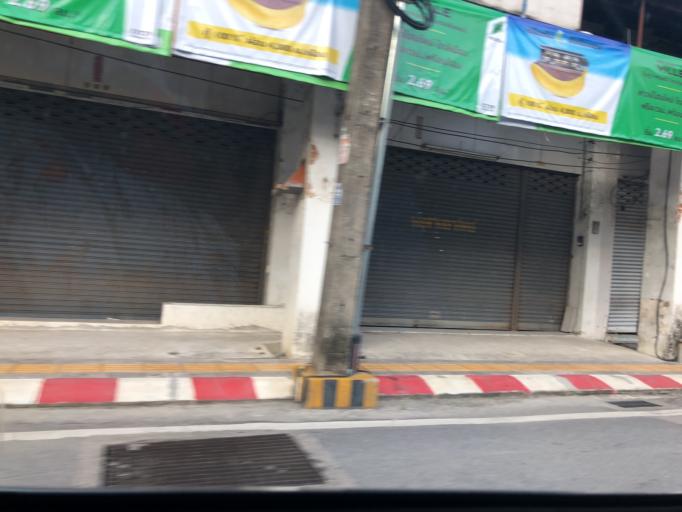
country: TH
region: Phuket
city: Ban Talat Nua
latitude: 7.8864
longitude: 98.3905
